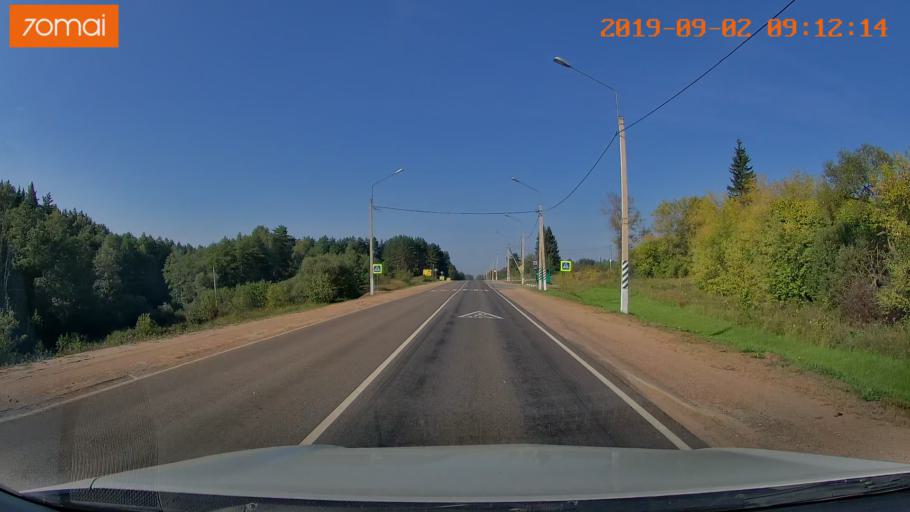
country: RU
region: Kaluga
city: Nikola-Lenivets
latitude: 54.8622
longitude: 35.5604
